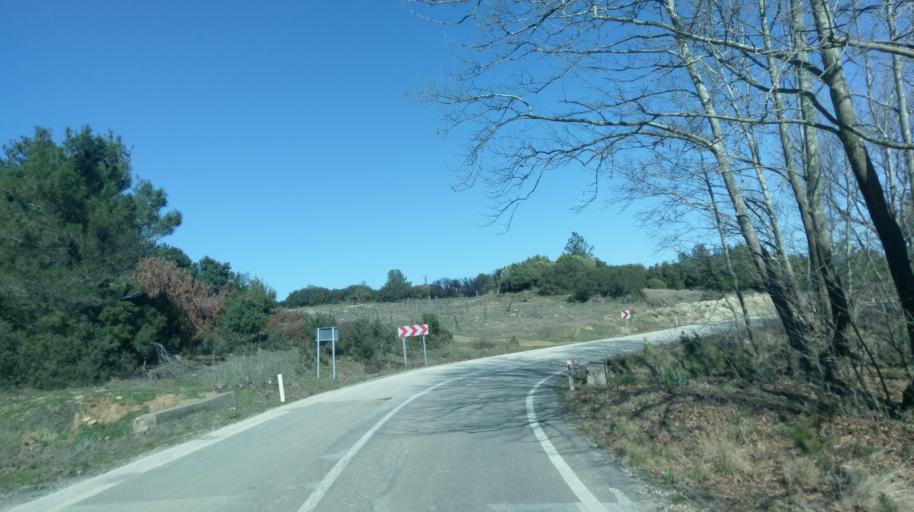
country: TR
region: Canakkale
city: Eceabat
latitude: 40.1214
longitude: 26.2571
